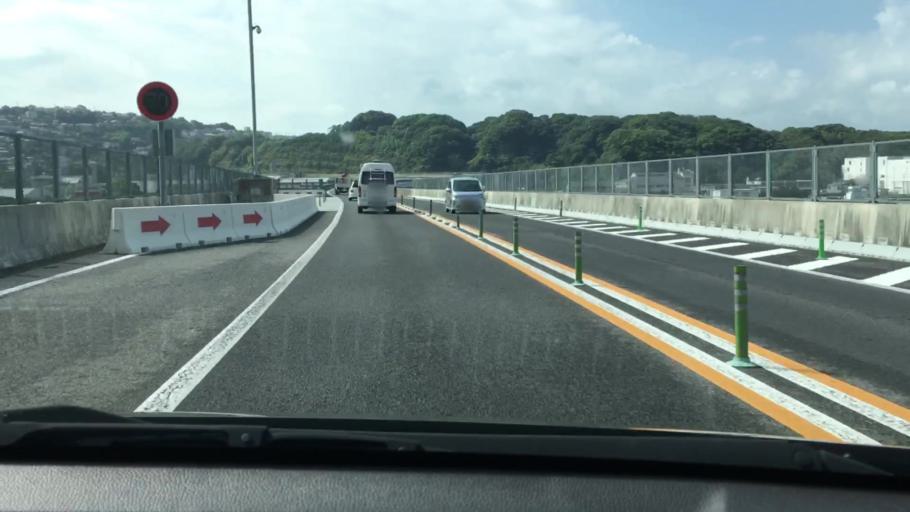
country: JP
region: Nagasaki
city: Sasebo
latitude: 33.1595
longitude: 129.7289
